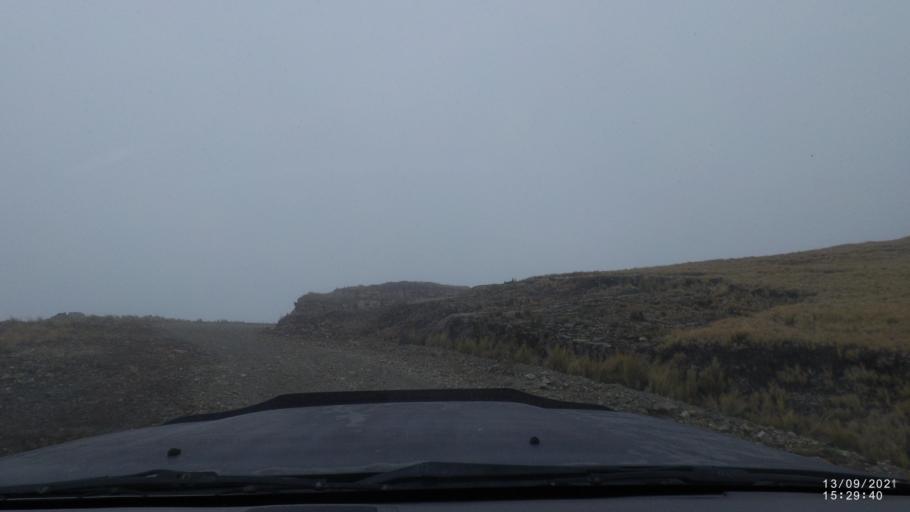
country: BO
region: Cochabamba
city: Colomi
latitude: -17.3452
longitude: -65.7581
